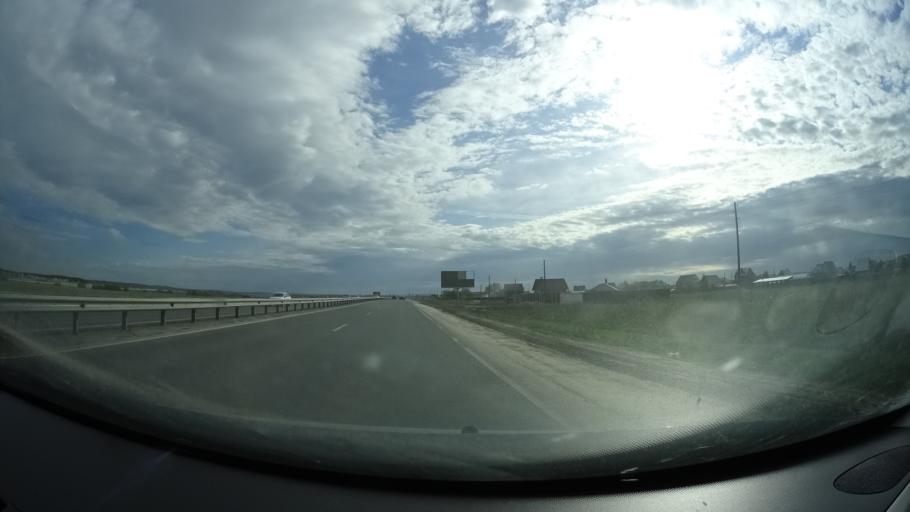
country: RU
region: Perm
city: Kultayevo
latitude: 57.9127
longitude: 55.9967
